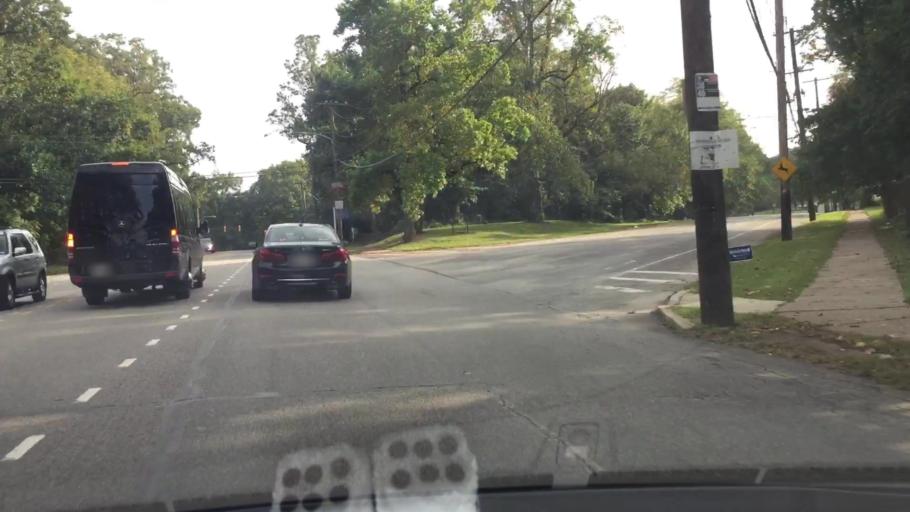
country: US
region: Pennsylvania
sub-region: Montgomery County
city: Bala-Cynwyd
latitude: 39.9945
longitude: -75.2182
